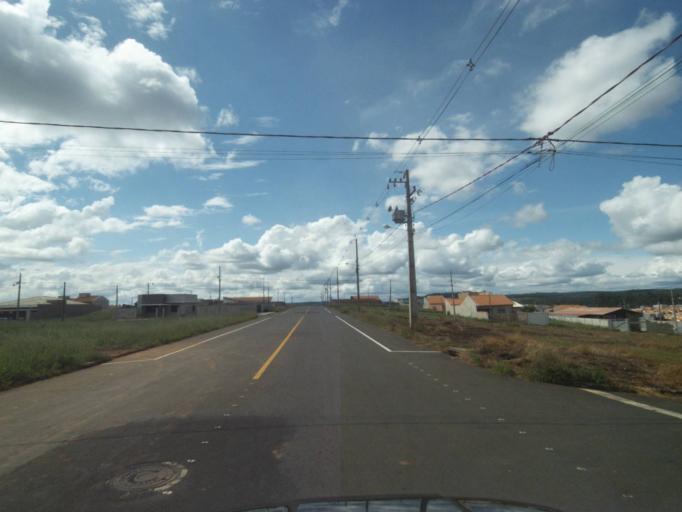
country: BR
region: Parana
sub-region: Telemaco Borba
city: Telemaco Borba
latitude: -24.3122
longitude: -50.6383
